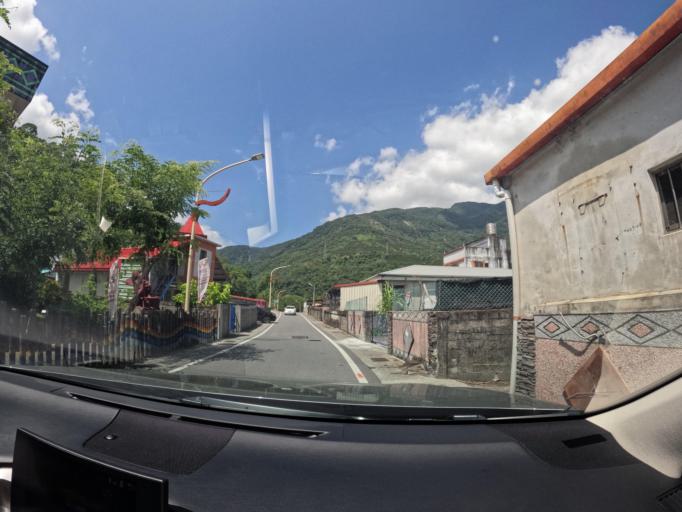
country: TW
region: Taiwan
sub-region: Hualien
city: Hualian
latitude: 23.7167
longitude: 121.4091
